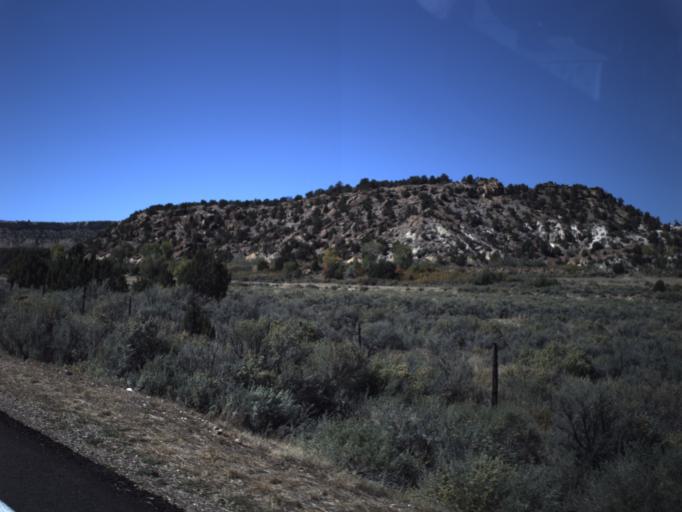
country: US
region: Utah
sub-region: Wayne County
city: Loa
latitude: 37.7746
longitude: -111.6439
